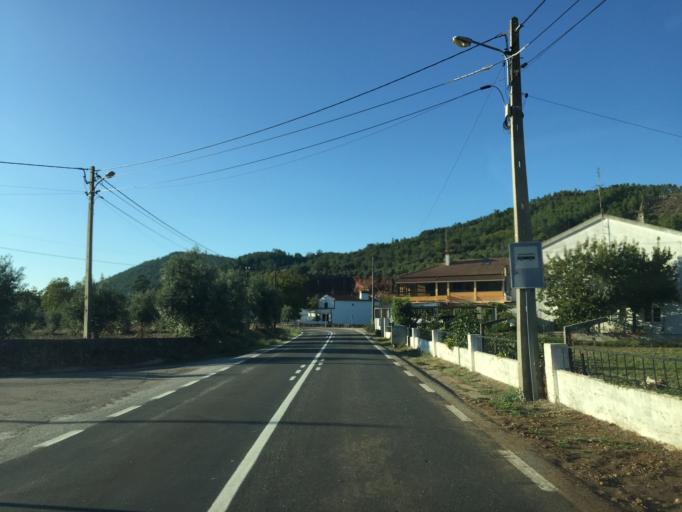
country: PT
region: Portalegre
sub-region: Marvao
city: Marvao
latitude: 39.3854
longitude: -7.3987
